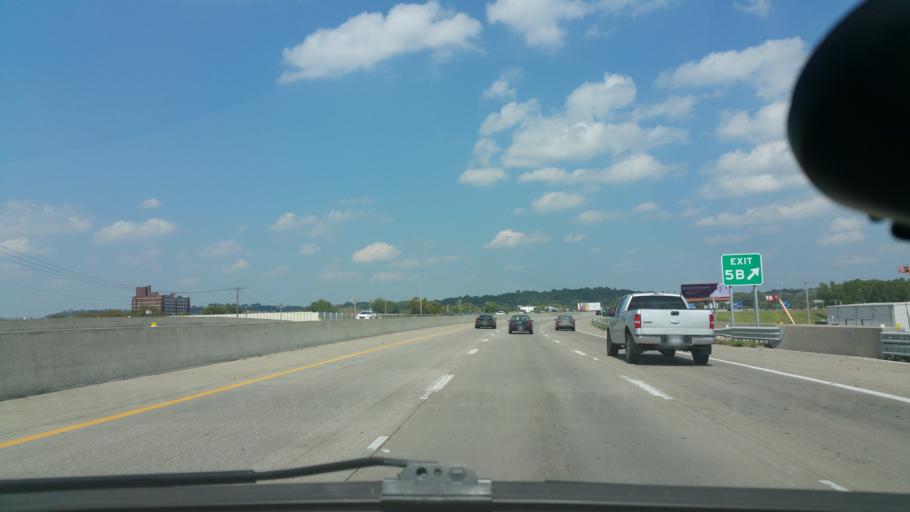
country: US
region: Missouri
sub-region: Clay County
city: North Kansas City
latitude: 39.1352
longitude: -94.5678
